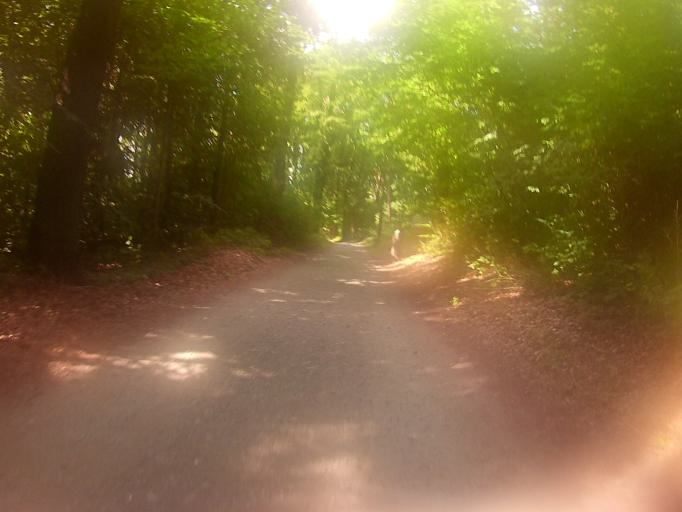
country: DE
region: Mecklenburg-Vorpommern
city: Koserow
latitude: 54.0572
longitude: 14.0015
